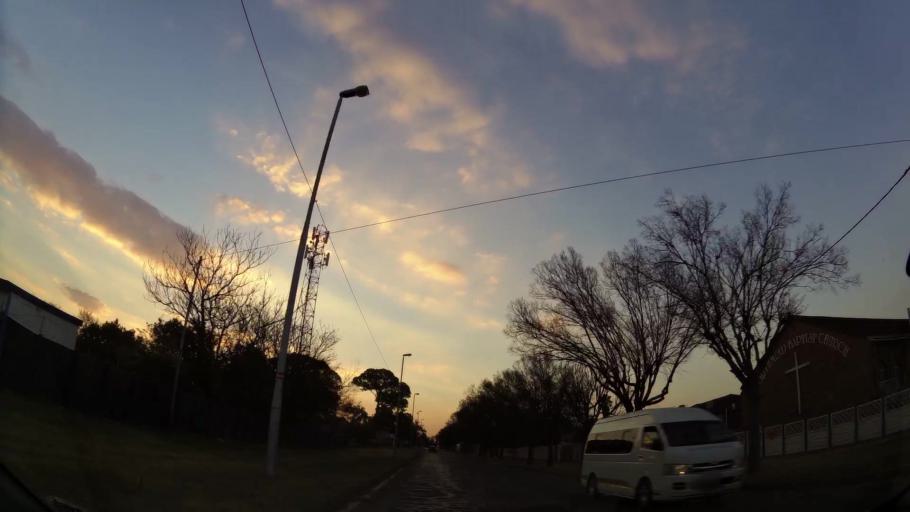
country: ZA
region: Gauteng
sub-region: Ekurhuleni Metropolitan Municipality
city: Benoni
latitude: -26.1670
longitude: 28.3146
